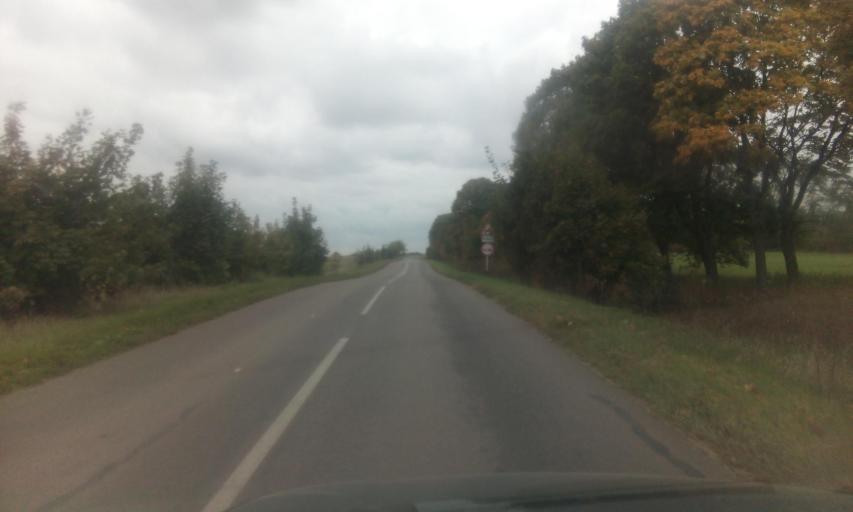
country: RU
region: Tula
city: Dubovka
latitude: 53.9585
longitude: 38.0758
